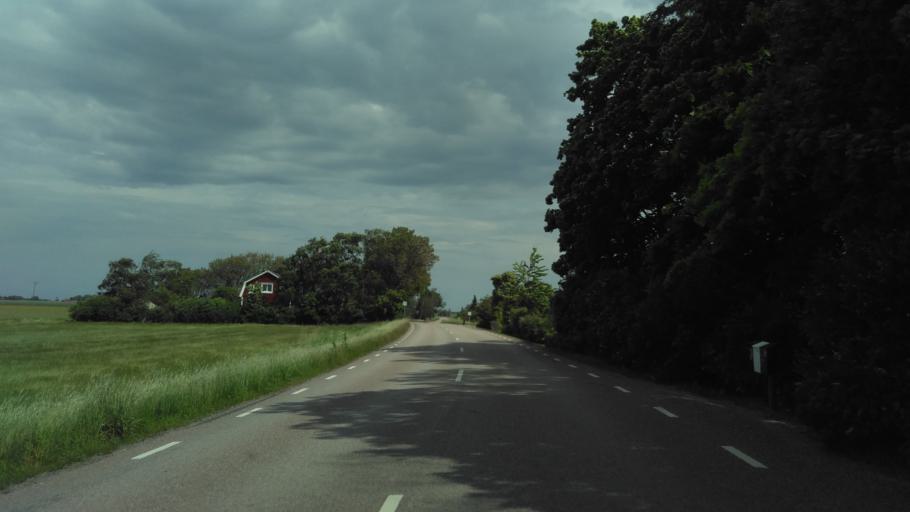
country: SE
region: Vaestra Goetaland
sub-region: Vara Kommun
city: Kvanum
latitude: 58.3560
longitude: 13.1352
